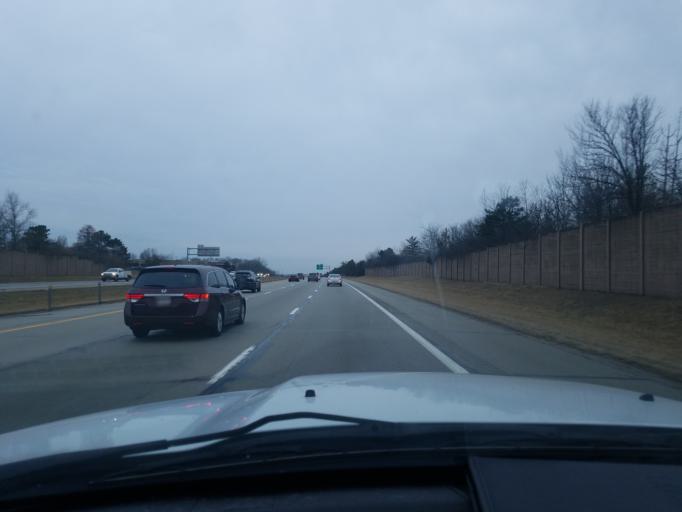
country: US
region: Ohio
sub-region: Montgomery County
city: Centerville
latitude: 39.6531
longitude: -84.1324
